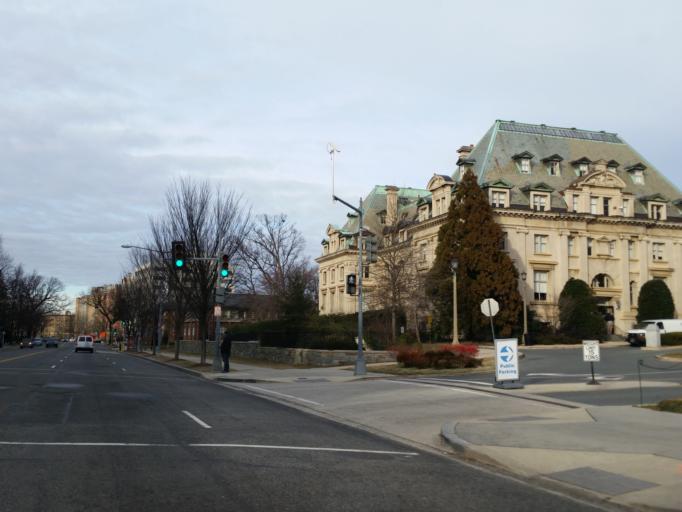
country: US
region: Maryland
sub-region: Montgomery County
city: Friendship Village
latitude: 38.9306
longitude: -77.0728
